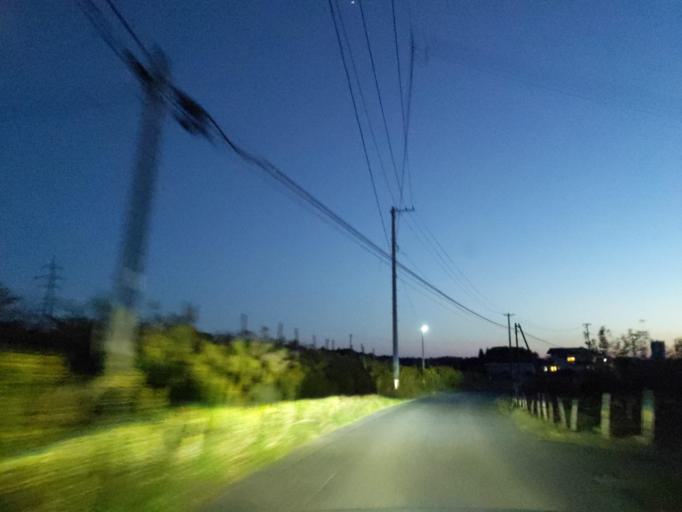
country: JP
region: Fukushima
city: Sukagawa
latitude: 37.3202
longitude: 140.3911
